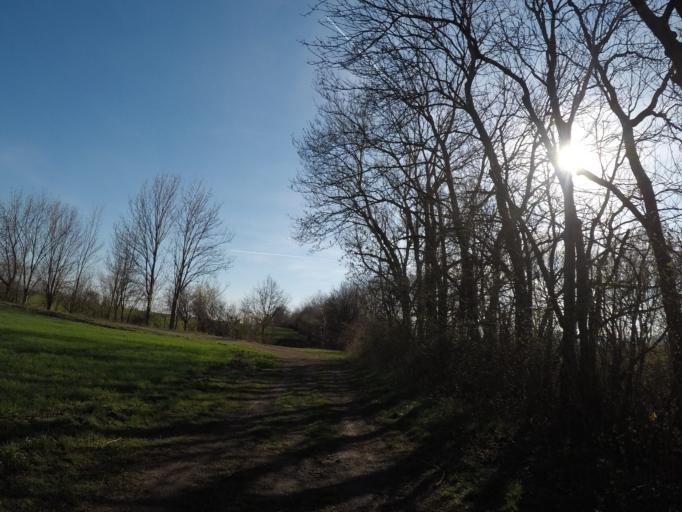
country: AT
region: Lower Austria
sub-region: Politischer Bezirk Modling
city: Vosendorf
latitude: 48.1014
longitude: 16.3321
